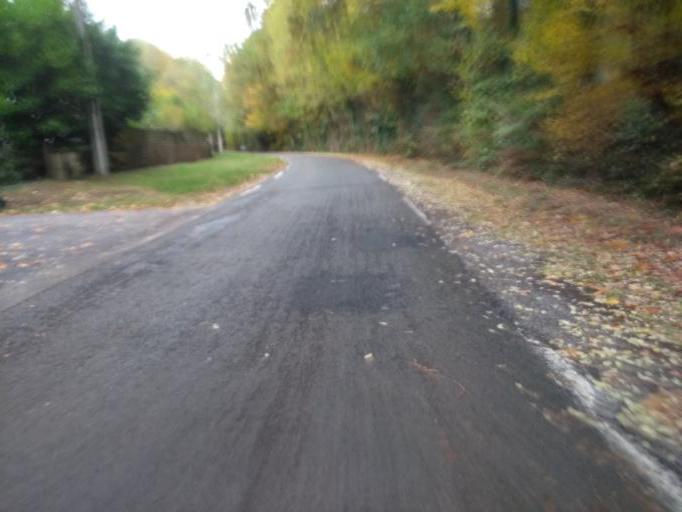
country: FR
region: Aquitaine
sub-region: Departement de la Gironde
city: Gradignan
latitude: 44.7618
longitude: -0.6047
